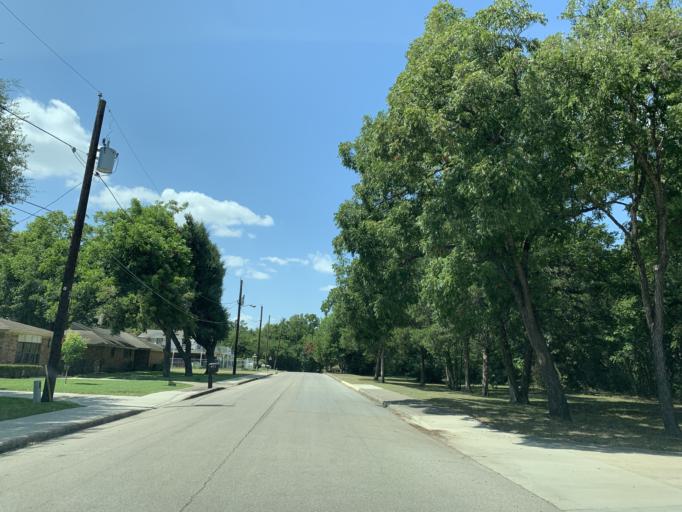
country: US
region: Texas
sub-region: Dallas County
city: Hutchins
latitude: 32.7096
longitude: -96.7652
